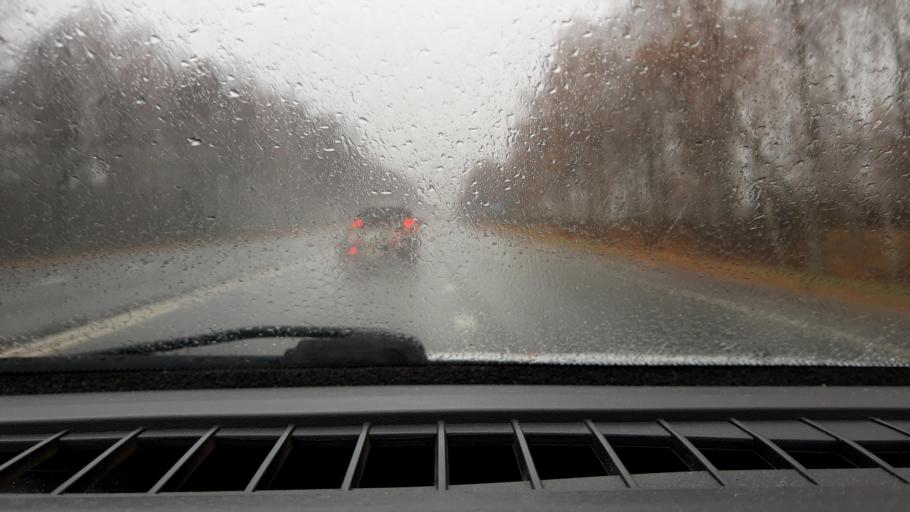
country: RU
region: Nizjnij Novgorod
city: Sitniki
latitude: 56.5241
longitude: 44.0262
